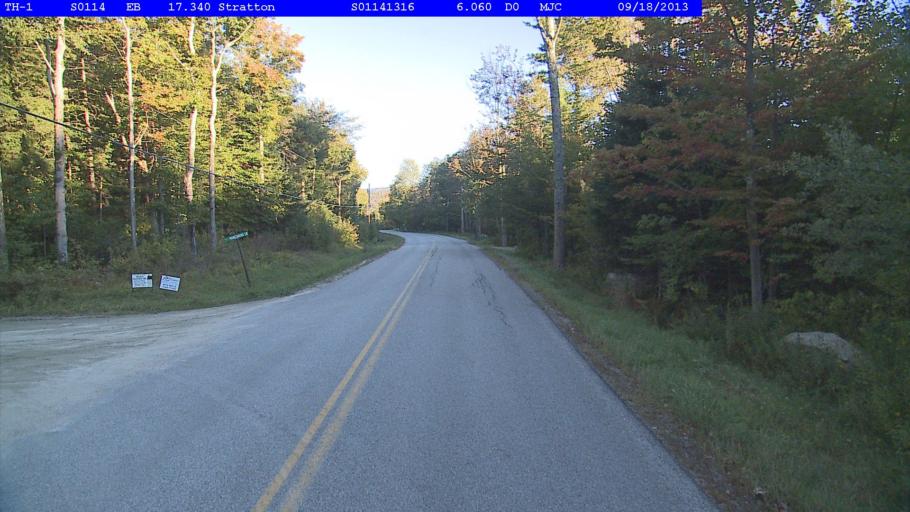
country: US
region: Vermont
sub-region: Windham County
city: Dover
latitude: 43.0360
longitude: -72.8968
